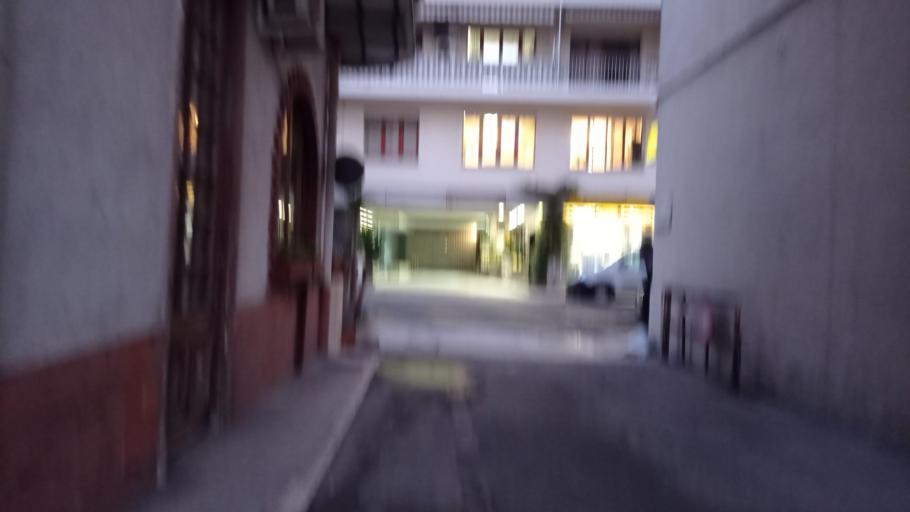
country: FR
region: Provence-Alpes-Cote d'Azur
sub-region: Departement des Alpes-Maritimes
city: Nice
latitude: 43.7012
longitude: 7.2605
